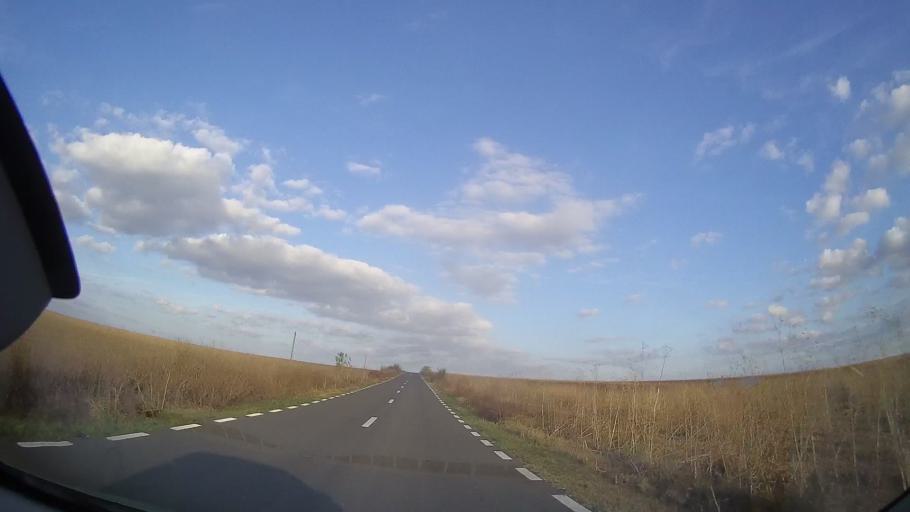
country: RO
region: Constanta
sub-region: Comuna Independenta
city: Independenta
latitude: 43.9376
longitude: 28.0377
